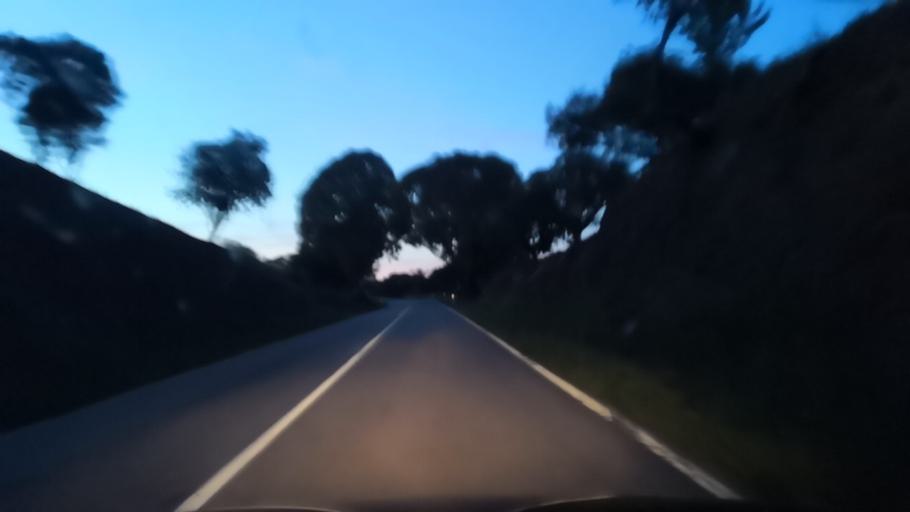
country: ES
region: Extremadura
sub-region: Provincia de Caceres
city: Piedras Albas
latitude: 39.8487
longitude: -6.9819
